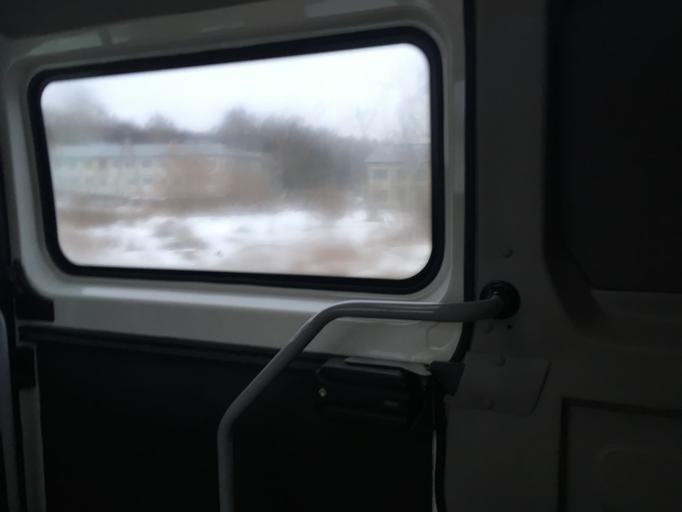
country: RU
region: Tula
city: Dubna
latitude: 54.1023
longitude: 37.1073
